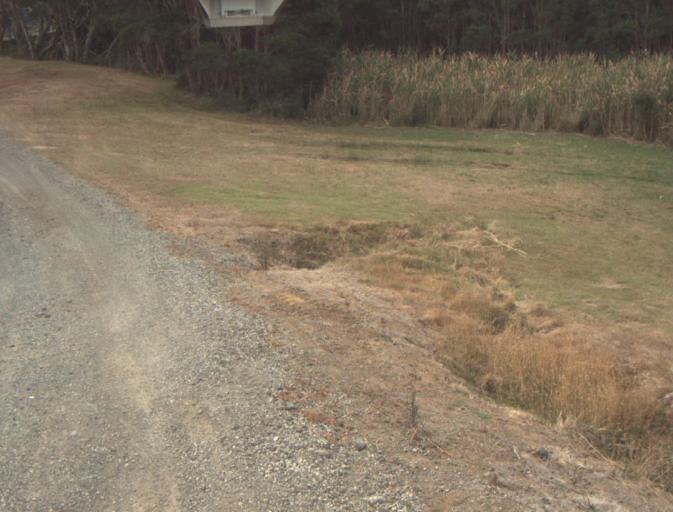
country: AU
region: Tasmania
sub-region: Launceston
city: Mayfield
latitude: -41.2784
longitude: 147.0170
